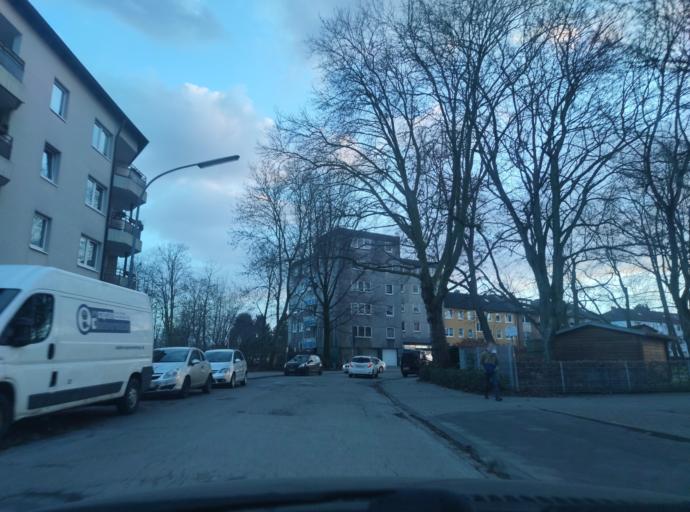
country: DE
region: North Rhine-Westphalia
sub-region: Regierungsbezirk Munster
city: Gelsenkirchen
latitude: 51.4911
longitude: 7.0925
